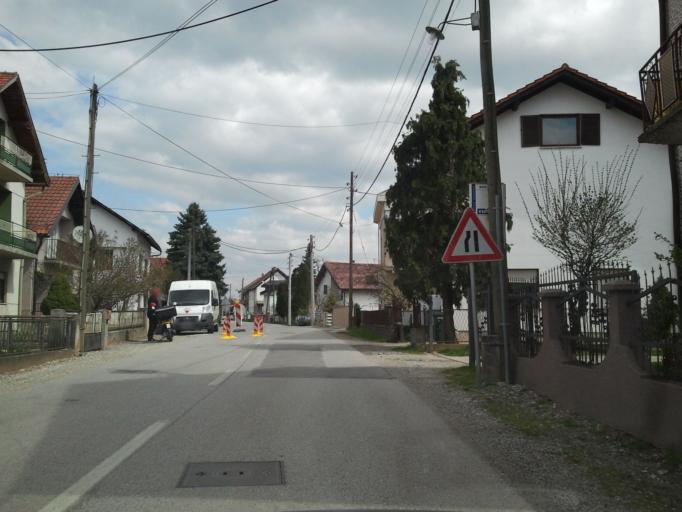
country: HR
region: Grad Zagreb
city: Odra
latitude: 45.7441
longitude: 15.9583
